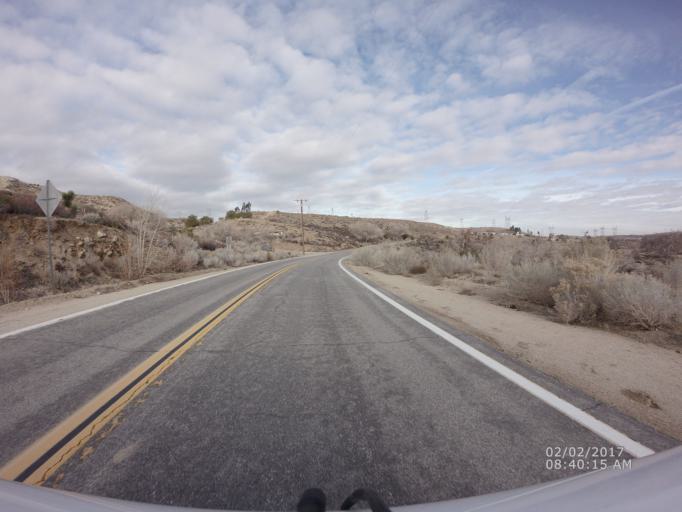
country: US
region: California
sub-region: Los Angeles County
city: Littlerock
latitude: 34.4992
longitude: -118.0301
